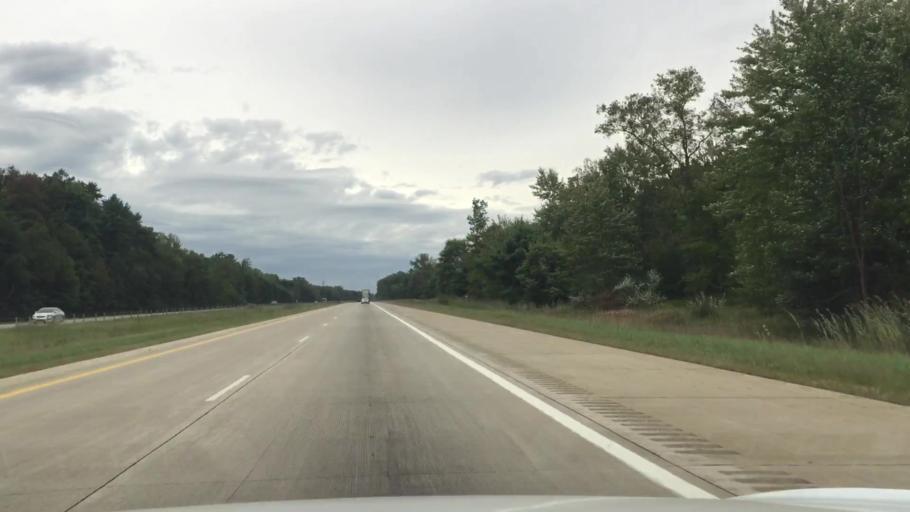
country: US
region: Michigan
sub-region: Saint Clair County
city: Saint Clair
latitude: 42.8345
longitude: -82.5971
